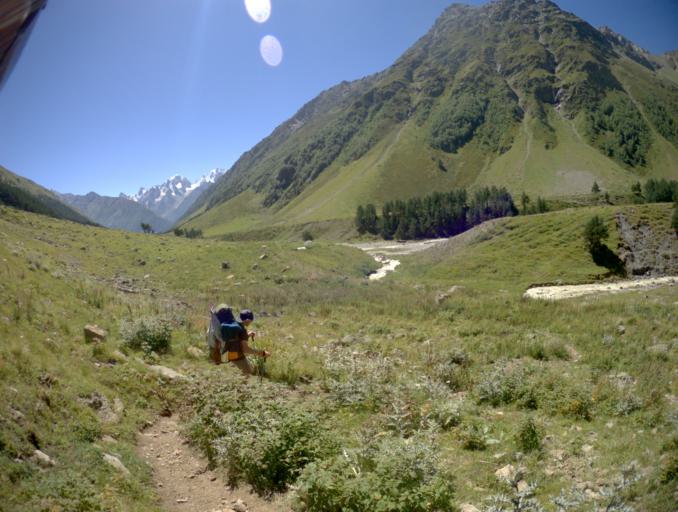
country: RU
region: Kabardino-Balkariya
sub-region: El'brusskiy Rayon
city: El'brus
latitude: 43.2924
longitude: 42.5955
